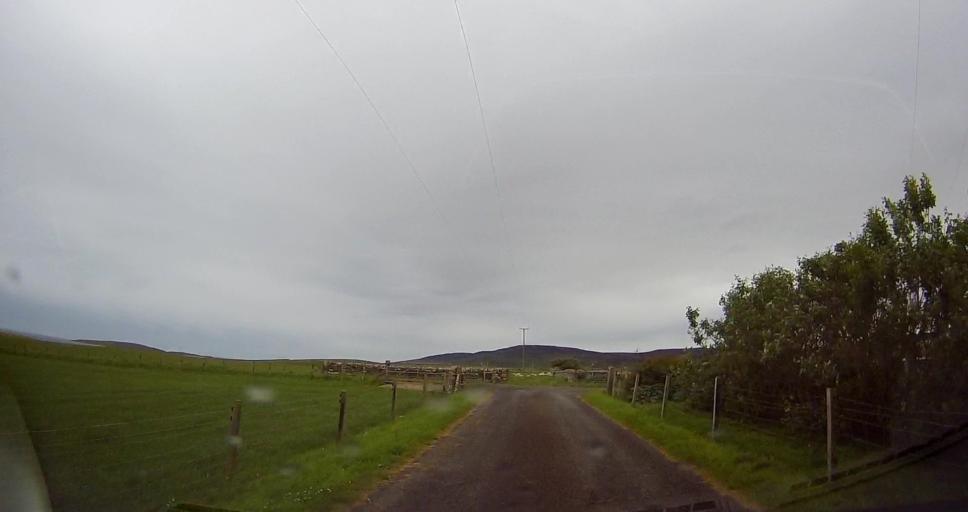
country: GB
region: Scotland
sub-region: Orkney Islands
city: Orkney
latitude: 59.1163
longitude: -3.0754
